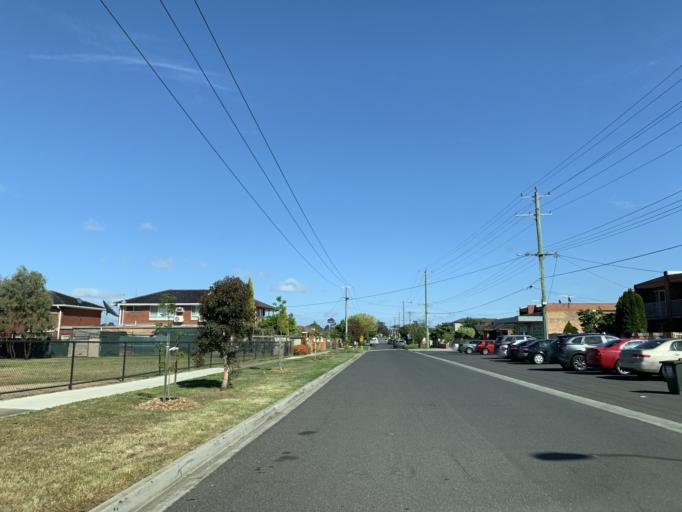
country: AU
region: Victoria
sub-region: Brimbank
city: Kealba
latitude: -37.7375
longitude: 144.8157
